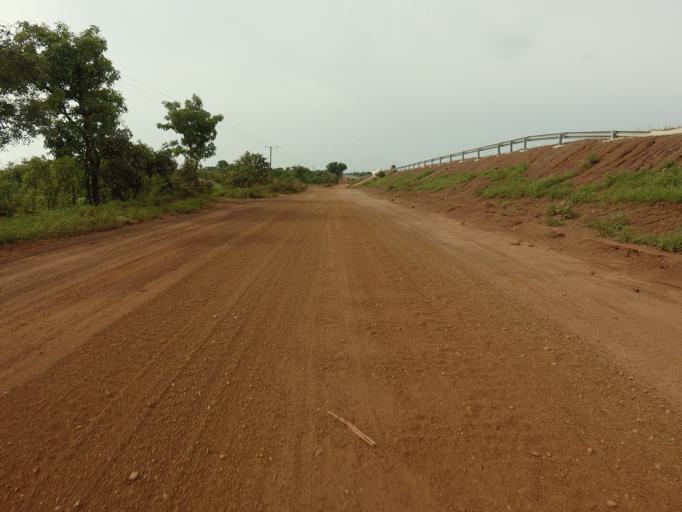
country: GH
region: Northern
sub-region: Yendi
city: Yendi
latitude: 9.6558
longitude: -0.0724
